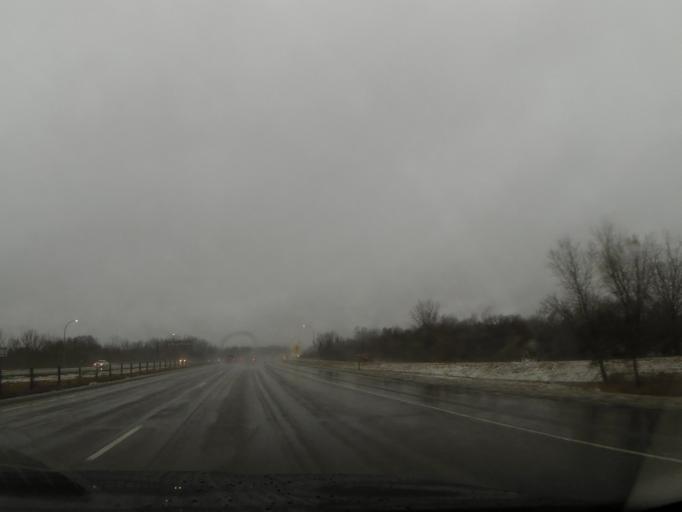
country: US
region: Minnesota
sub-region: Dakota County
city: Inver Grove Heights
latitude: 44.8631
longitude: -93.0595
